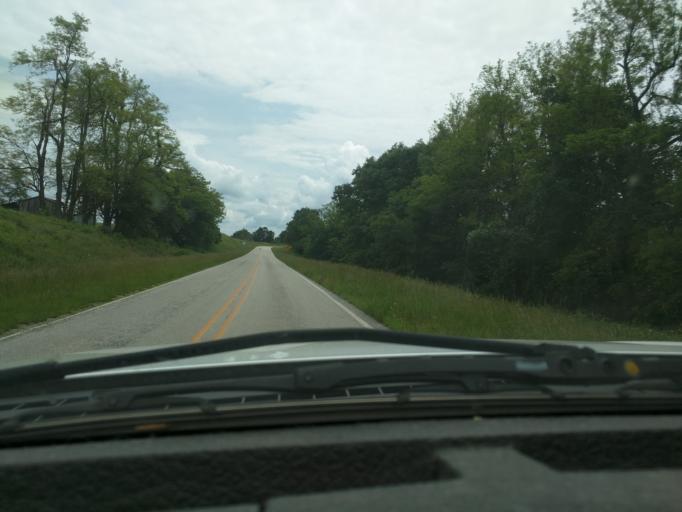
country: US
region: Arkansas
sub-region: Madison County
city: Huntsville
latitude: 35.8371
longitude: -93.5747
